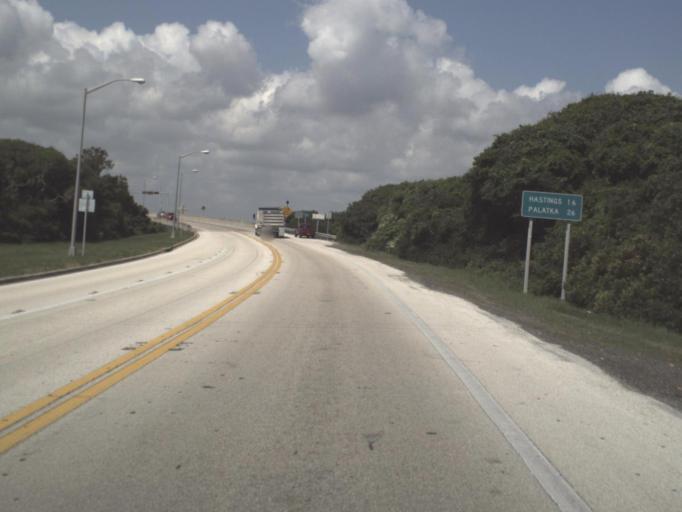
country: US
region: Florida
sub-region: Saint Johns County
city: Butler Beach
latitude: 29.7705
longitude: -81.2553
